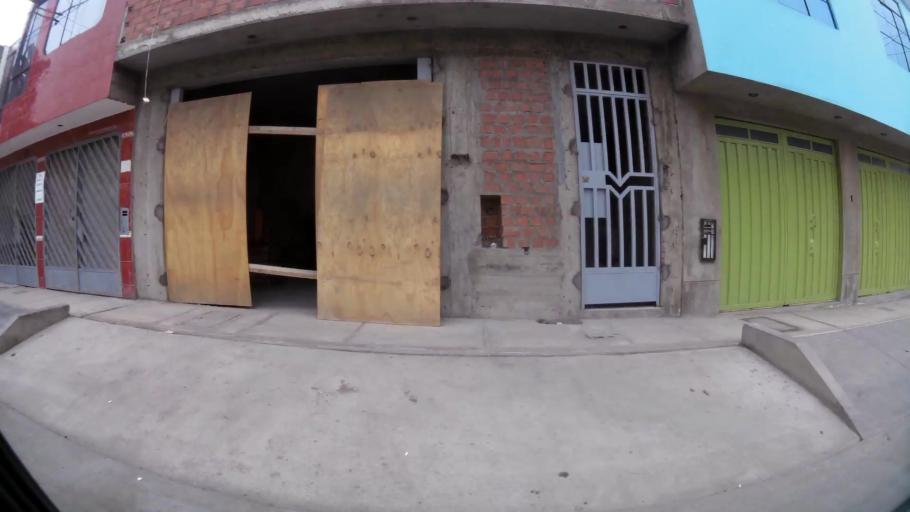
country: PE
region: Lima
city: Ventanilla
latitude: -11.9320
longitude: -77.0847
